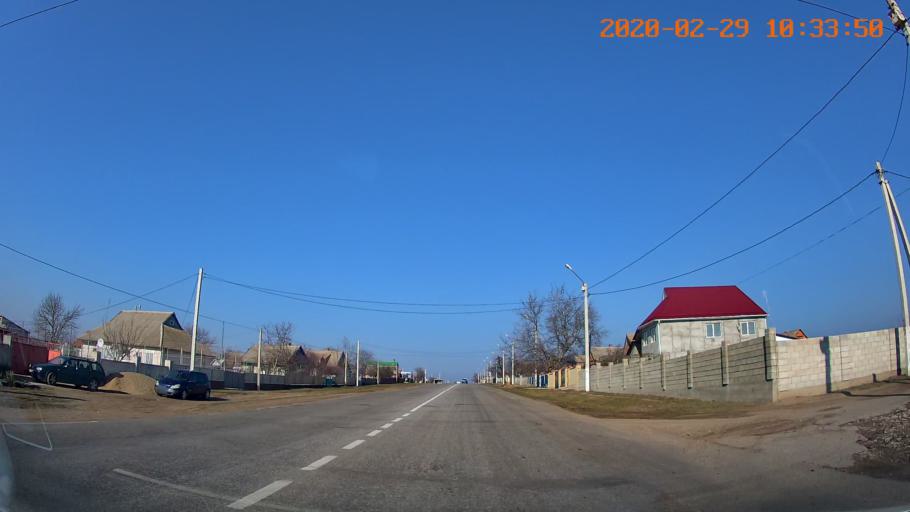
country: MD
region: Anenii Noi
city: Varnita
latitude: 46.9728
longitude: 29.5402
